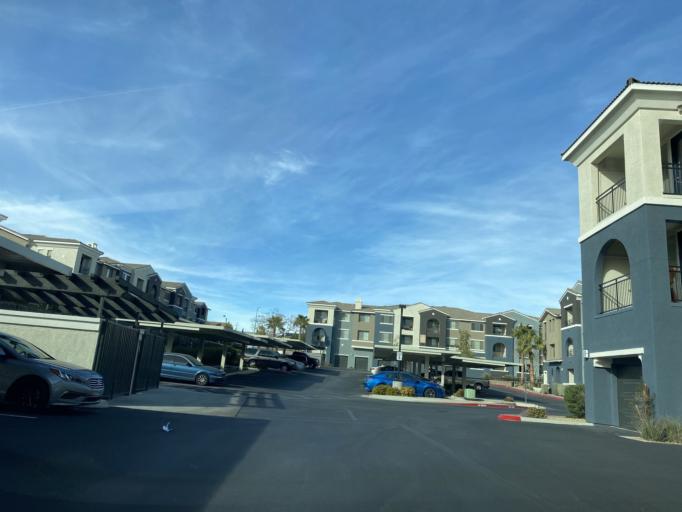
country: US
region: Nevada
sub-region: Clark County
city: Summerlin South
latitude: 36.2758
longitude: -115.3314
